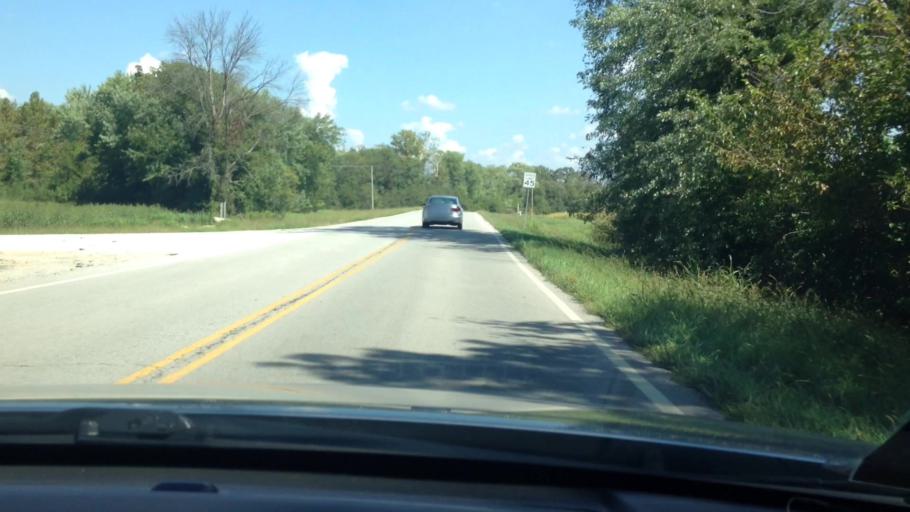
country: US
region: Missouri
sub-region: Platte County
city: Platte City
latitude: 39.3367
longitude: -94.8129
